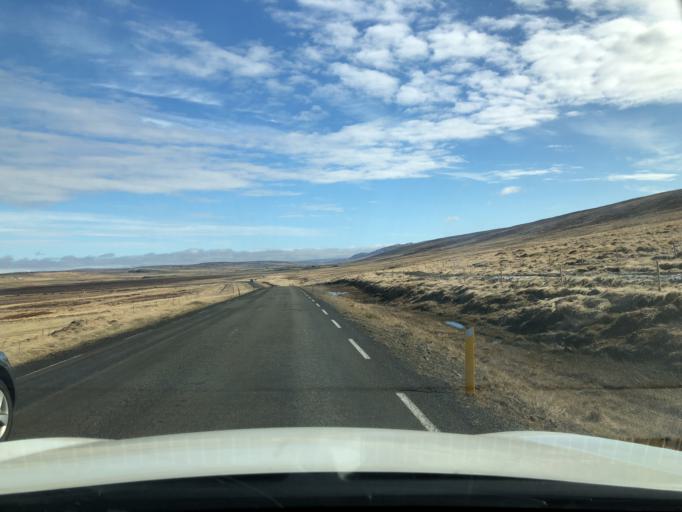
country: IS
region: West
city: Borgarnes
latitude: 65.0836
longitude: -21.7556
